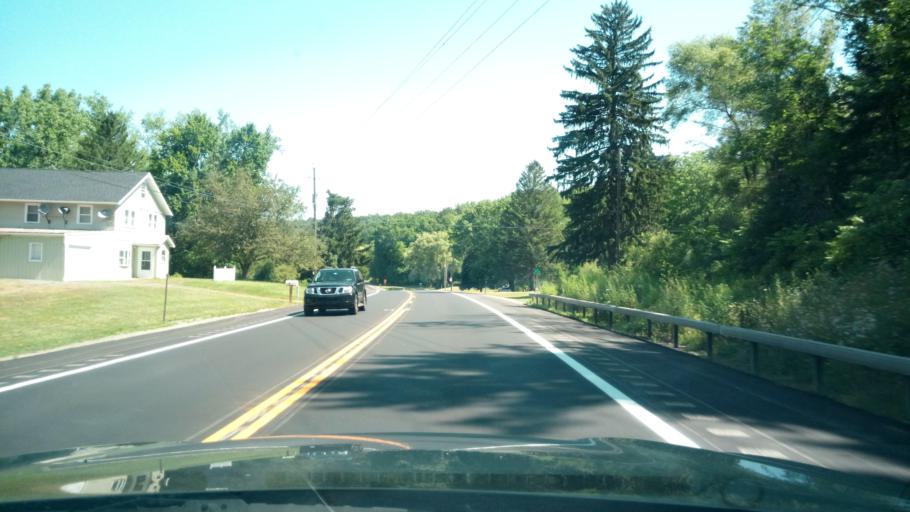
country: US
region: New York
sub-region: Schuyler County
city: Montour Falls
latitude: 42.3118
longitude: -76.8454
